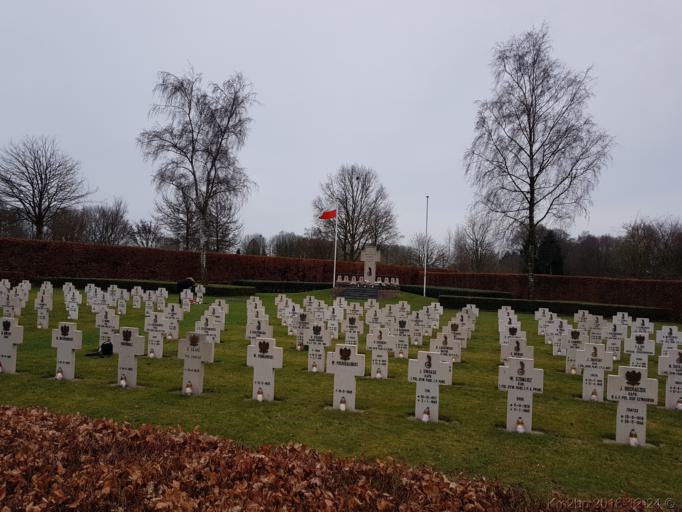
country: NL
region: North Brabant
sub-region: Gemeente Breda
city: Breda
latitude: 51.5825
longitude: 4.7475
